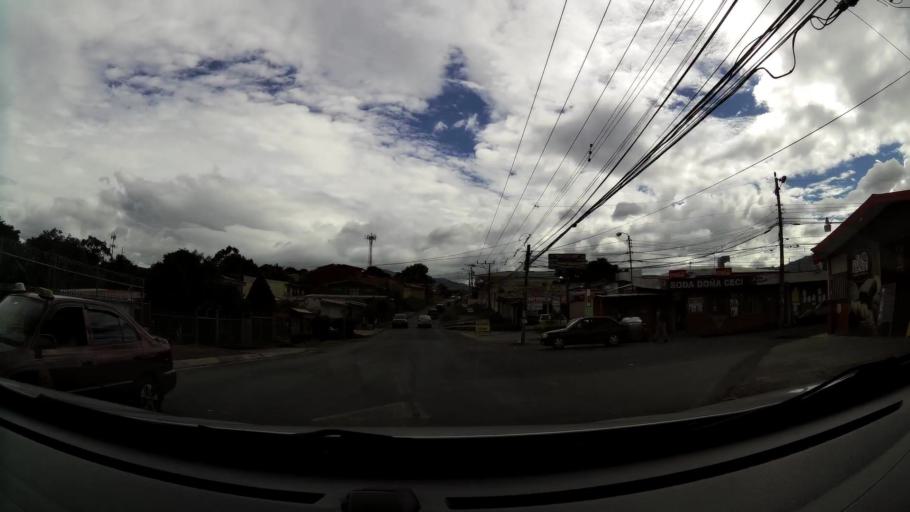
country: CR
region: San Jose
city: San Rafael Arriba
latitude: 9.8874
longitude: -84.0778
